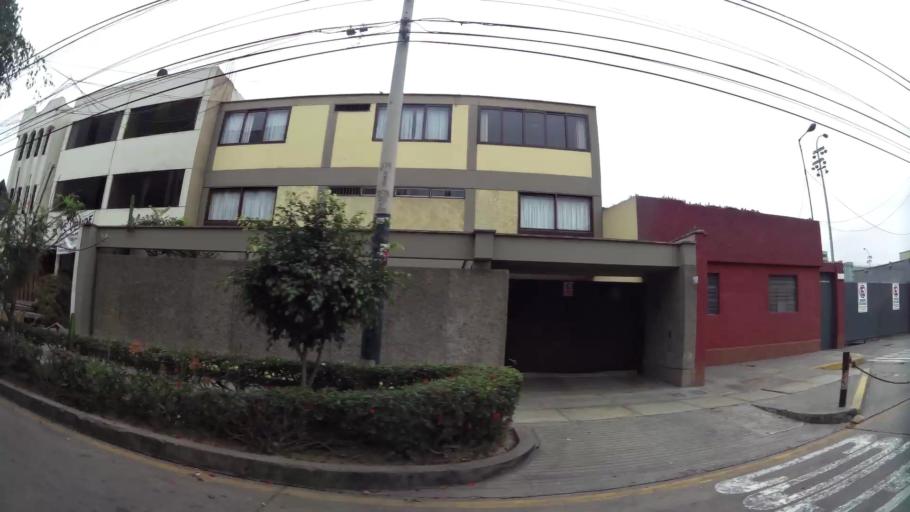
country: PE
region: Lima
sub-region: Lima
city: San Luis
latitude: -12.0928
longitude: -77.0203
